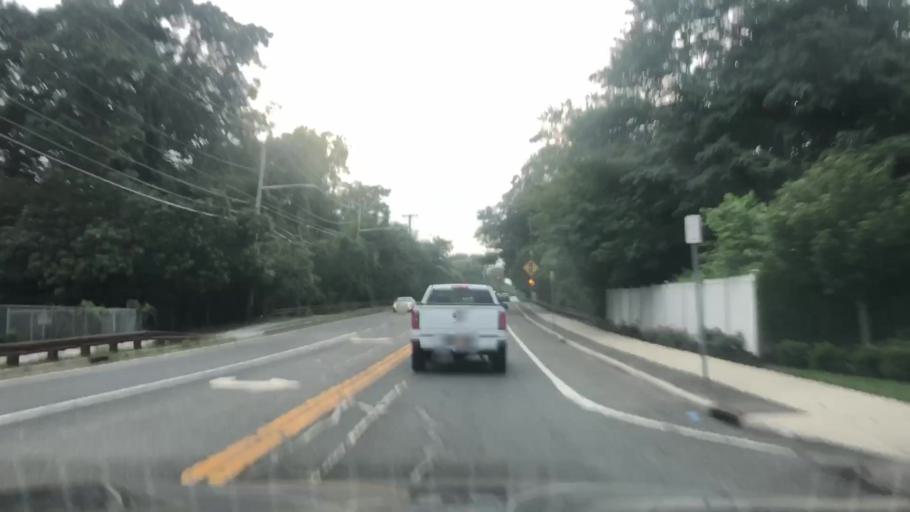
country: US
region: New York
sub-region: Nassau County
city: North Wantagh
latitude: 40.6924
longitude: -73.5165
